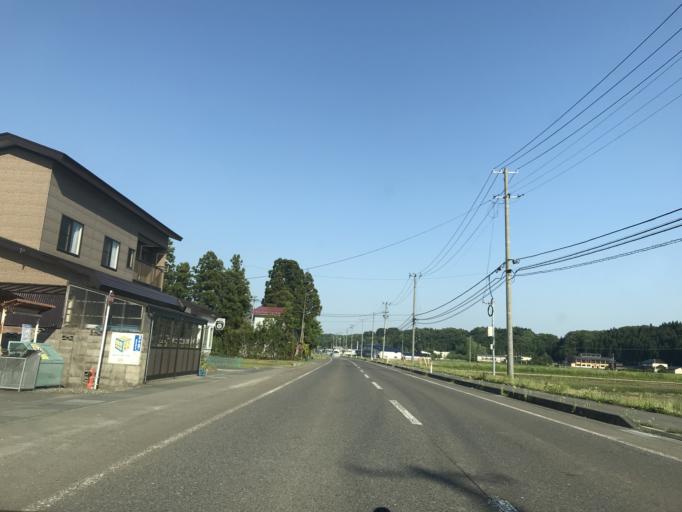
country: JP
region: Iwate
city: Kitakami
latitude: 39.2869
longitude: 141.0049
